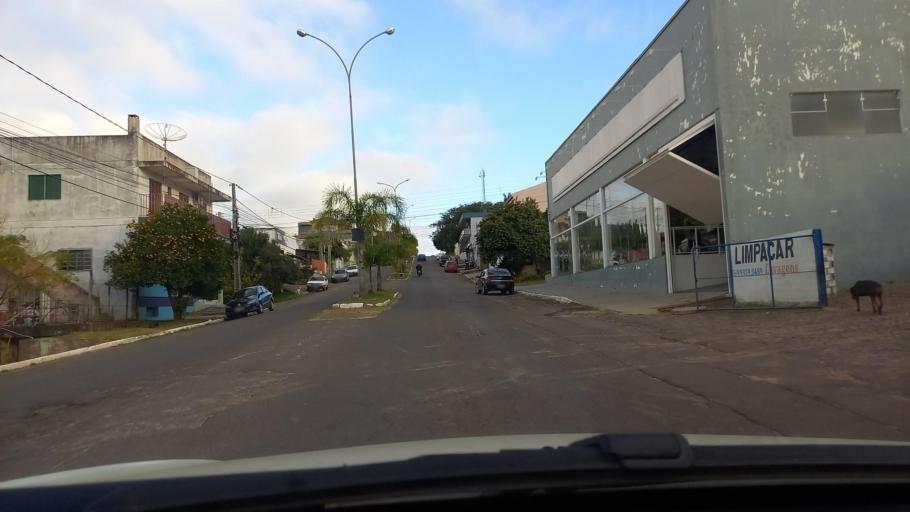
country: BR
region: Rio Grande do Sul
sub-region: Rosario Do Sul
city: Rosario do Sul
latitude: -30.2473
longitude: -54.9201
